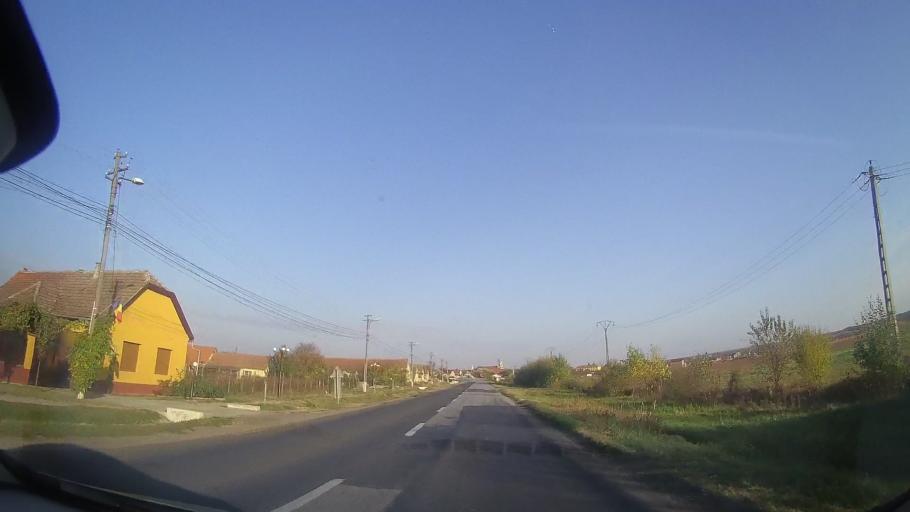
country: RO
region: Timis
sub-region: Comuna Pischia
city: Pischia
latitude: 45.8972
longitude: 21.3431
